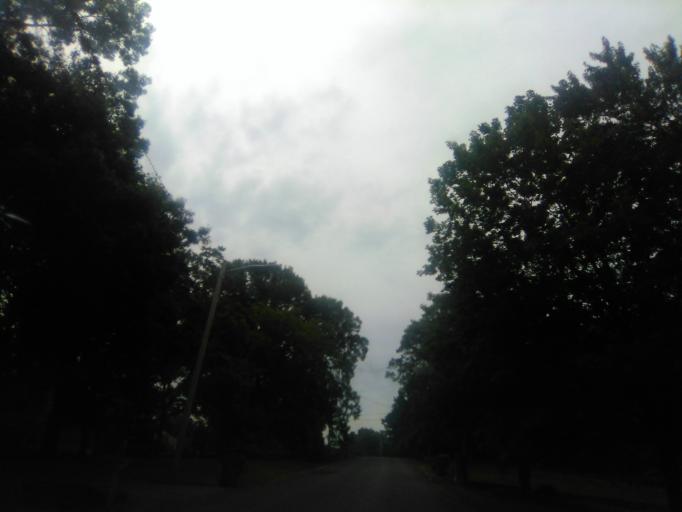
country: US
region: Tennessee
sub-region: Davidson County
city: Belle Meade
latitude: 36.1072
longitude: -86.8935
